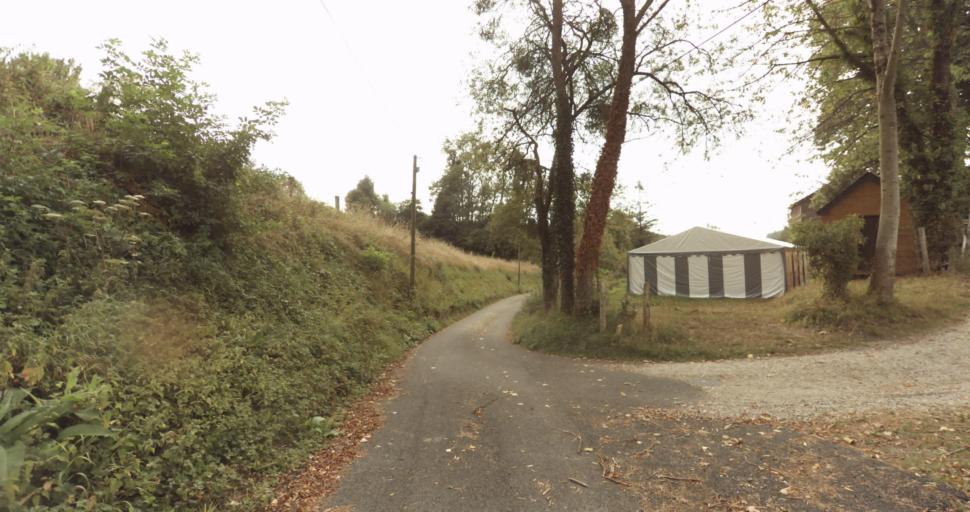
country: FR
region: Lower Normandy
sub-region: Departement de l'Orne
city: Vimoutiers
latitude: 48.9471
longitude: 0.2644
